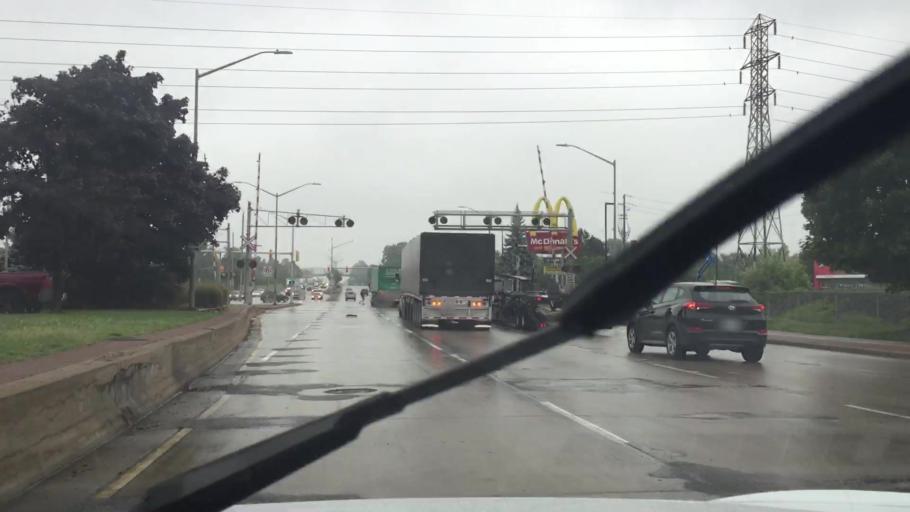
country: US
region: Michigan
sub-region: Wayne County
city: Detroit
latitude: 42.2997
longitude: -83.0657
